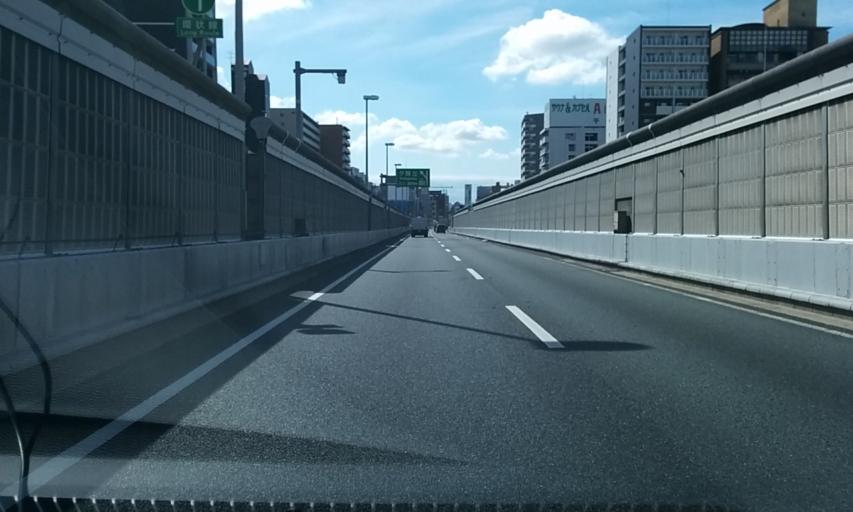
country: JP
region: Osaka
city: Osaka-shi
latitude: 34.6654
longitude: 135.5103
